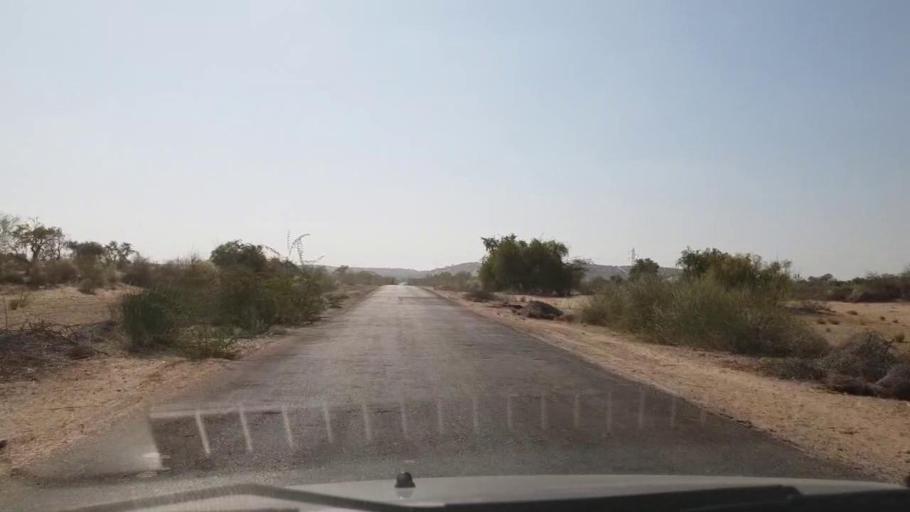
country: PK
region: Sindh
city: Mithi
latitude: 24.6542
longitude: 69.7532
